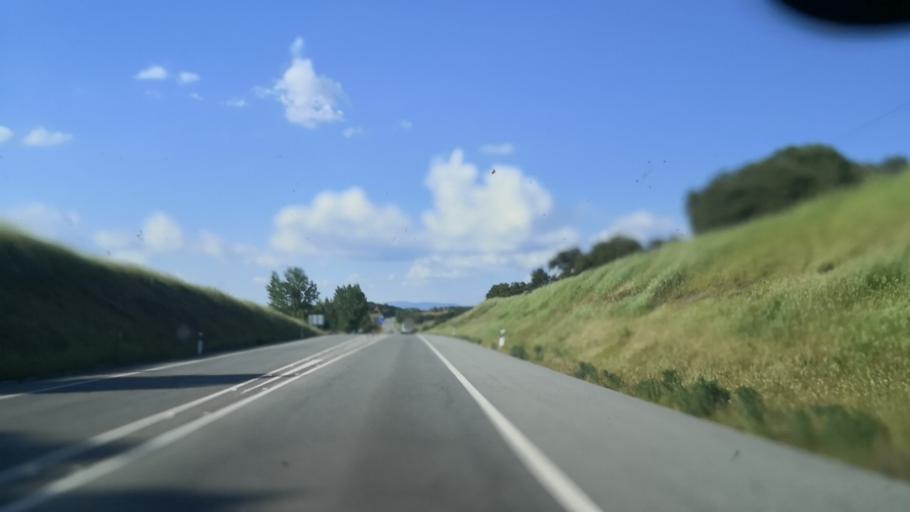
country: PT
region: Portalegre
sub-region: Arronches
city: Arronches
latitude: 39.0363
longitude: -7.4521
